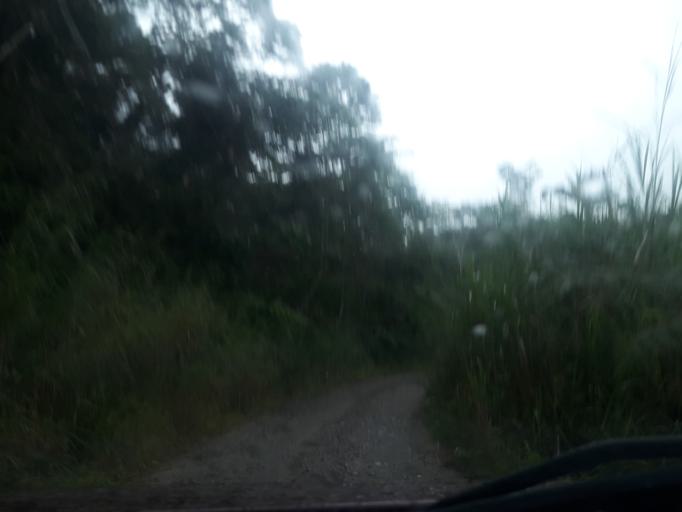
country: EC
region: Napo
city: Tena
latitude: -1.0992
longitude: -77.6930
